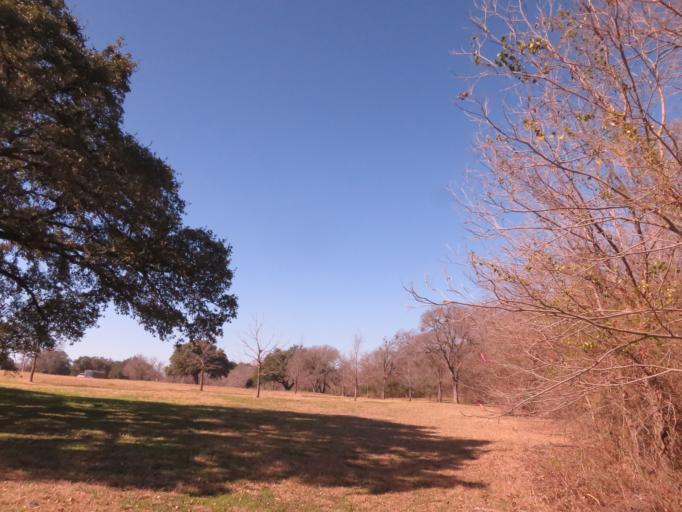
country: US
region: Texas
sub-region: Williamson County
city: Round Rock
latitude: 30.5296
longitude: -97.6313
